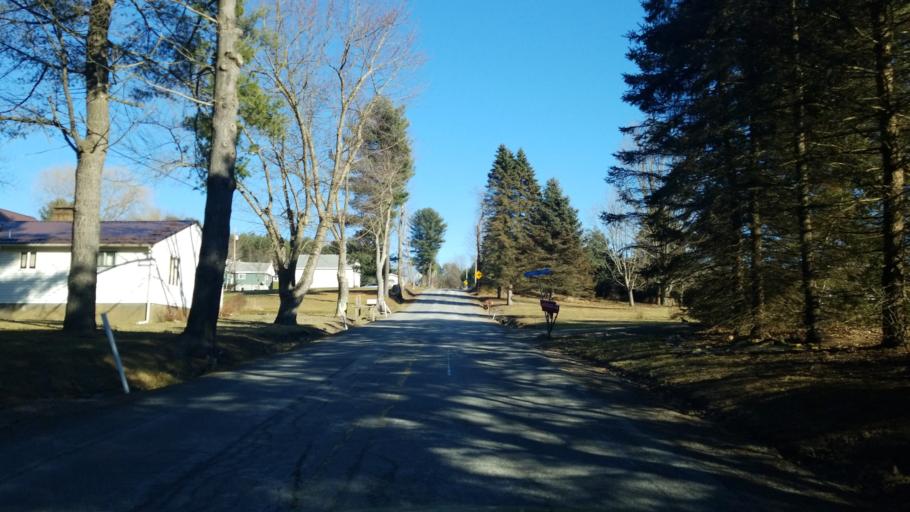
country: US
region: Pennsylvania
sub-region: Clearfield County
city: Sandy
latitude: 41.0478
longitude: -78.7593
